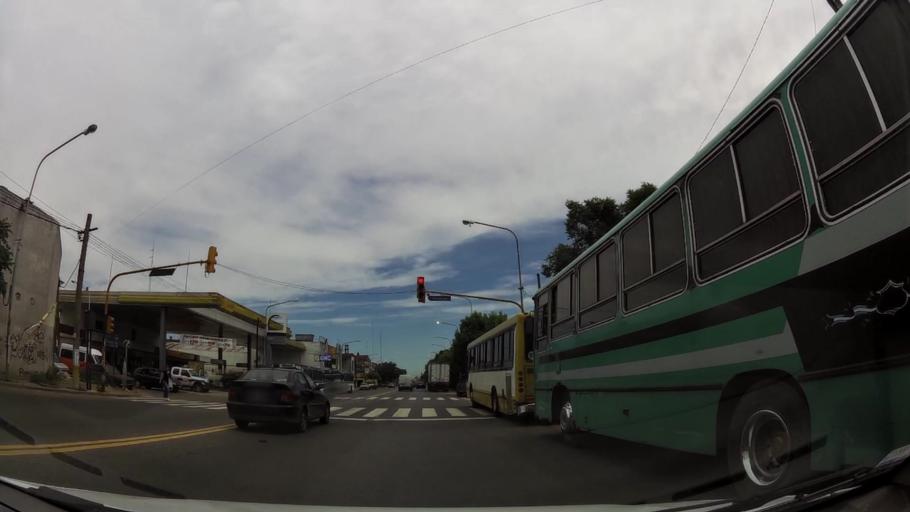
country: AR
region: Buenos Aires
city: San Justo
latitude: -34.6720
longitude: -58.5392
